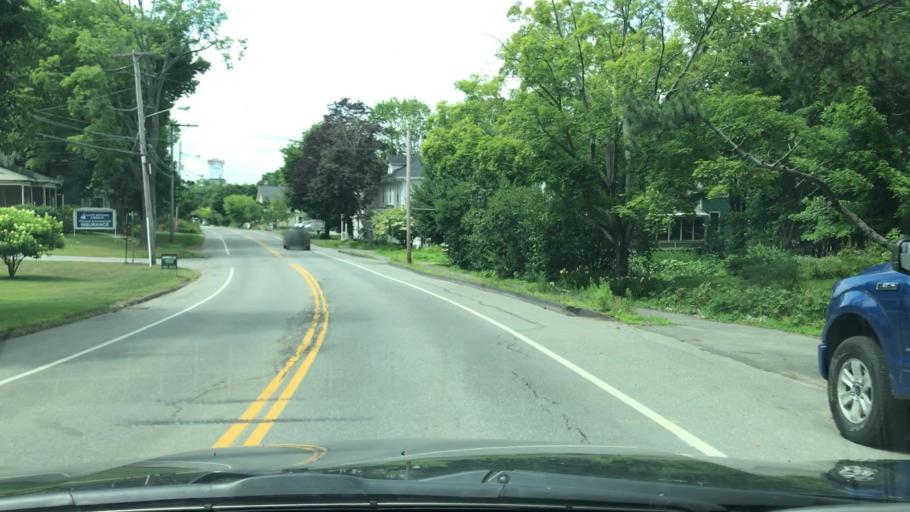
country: US
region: Maine
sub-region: Waldo County
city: Belfast
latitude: 44.4230
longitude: -69.0011
